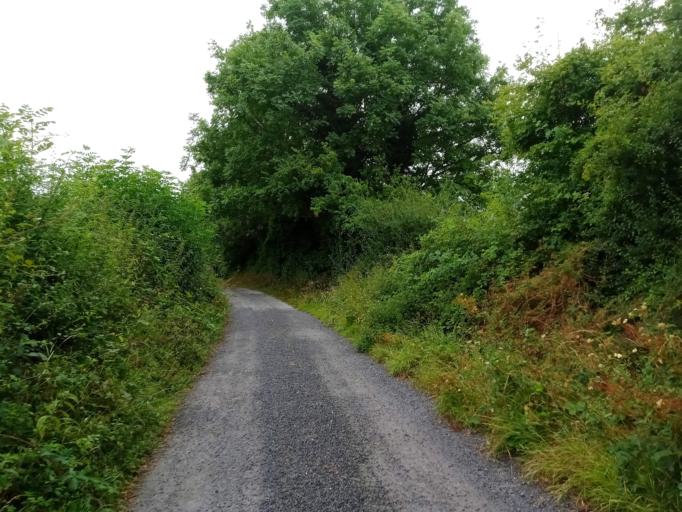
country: IE
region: Leinster
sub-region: Kilkenny
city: Ballyragget
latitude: 52.8113
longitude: -7.4308
